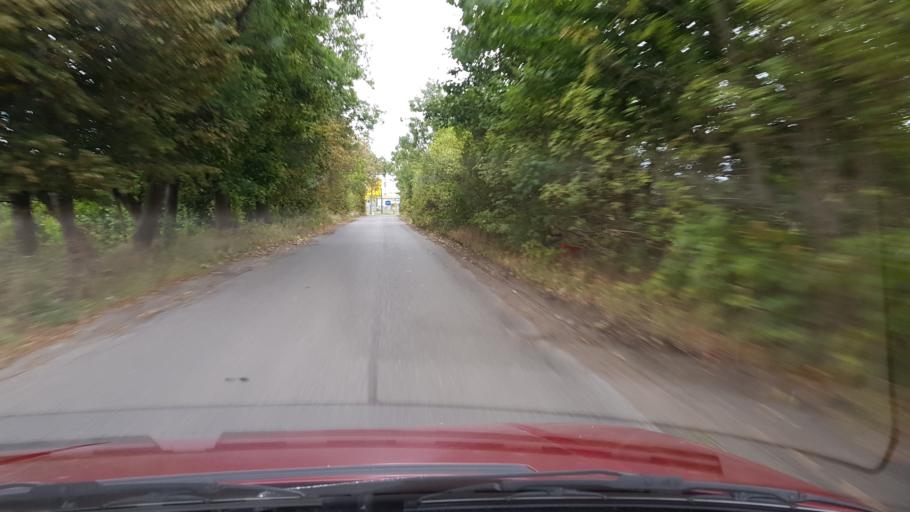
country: PL
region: West Pomeranian Voivodeship
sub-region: Koszalin
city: Koszalin
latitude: 54.1800
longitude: 16.1488
